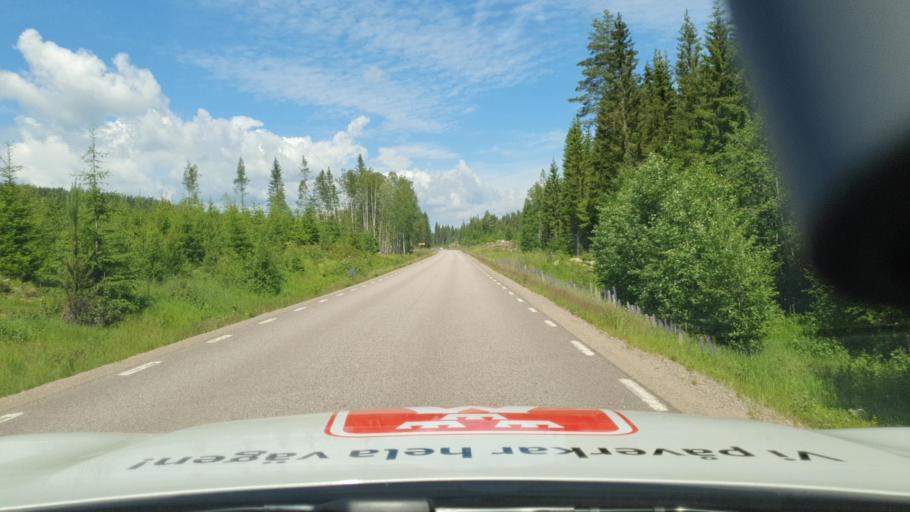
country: SE
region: Vaermland
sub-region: Torsby Kommun
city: Torsby
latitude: 60.4042
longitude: 12.9078
